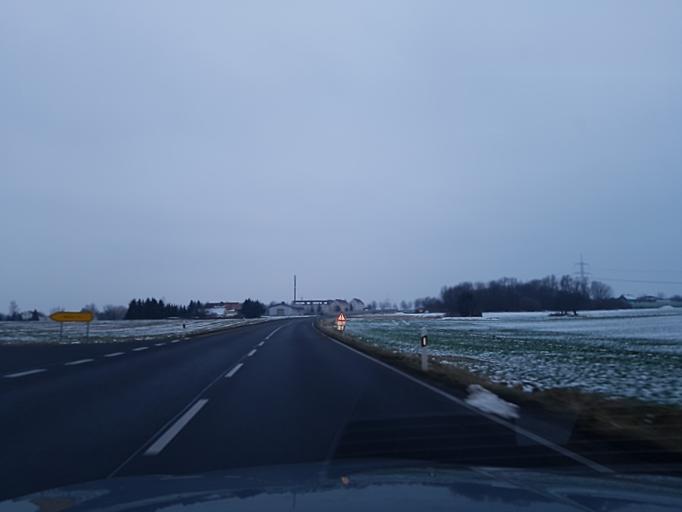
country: DE
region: Saxony
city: Ostrau
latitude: 51.2105
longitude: 13.1582
